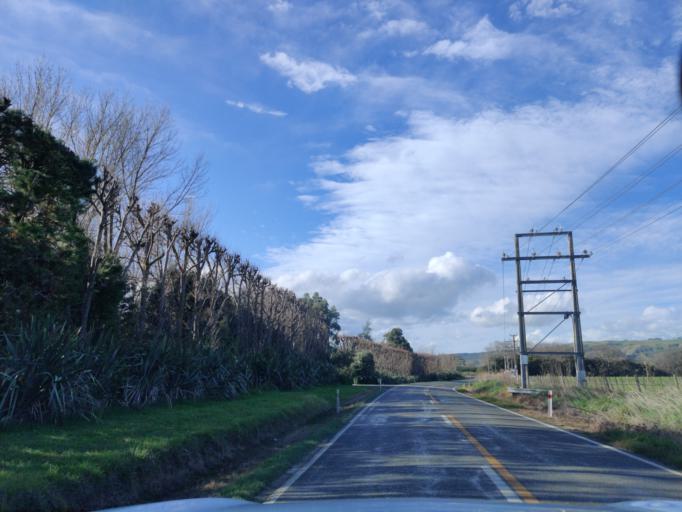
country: NZ
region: Manawatu-Wanganui
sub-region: Palmerston North City
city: Palmerston North
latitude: -40.3363
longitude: 175.7265
